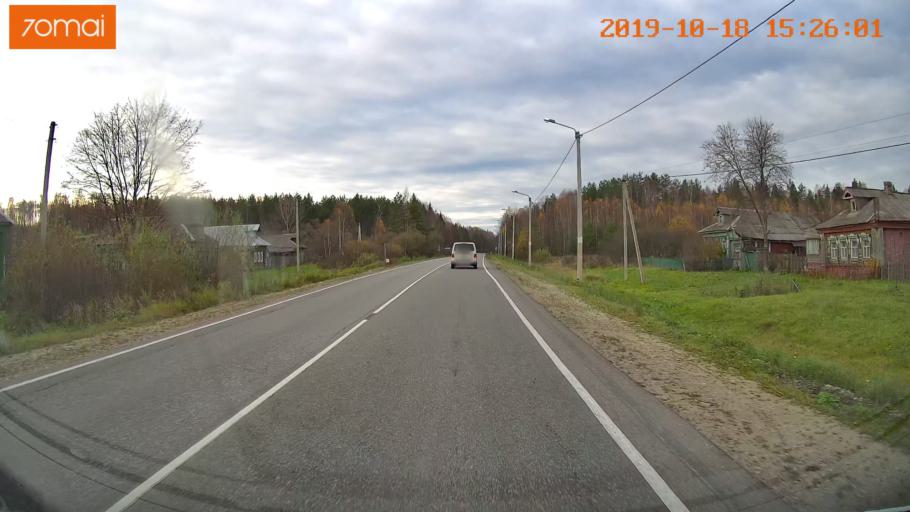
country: RU
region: Vladimir
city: Anopino
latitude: 55.7433
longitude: 40.6947
